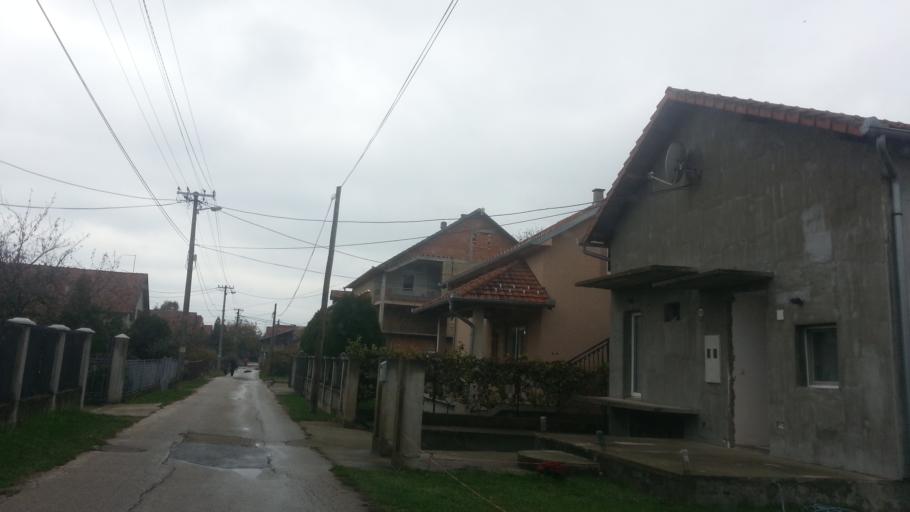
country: RS
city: Novi Banovci
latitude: 44.8989
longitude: 20.2955
